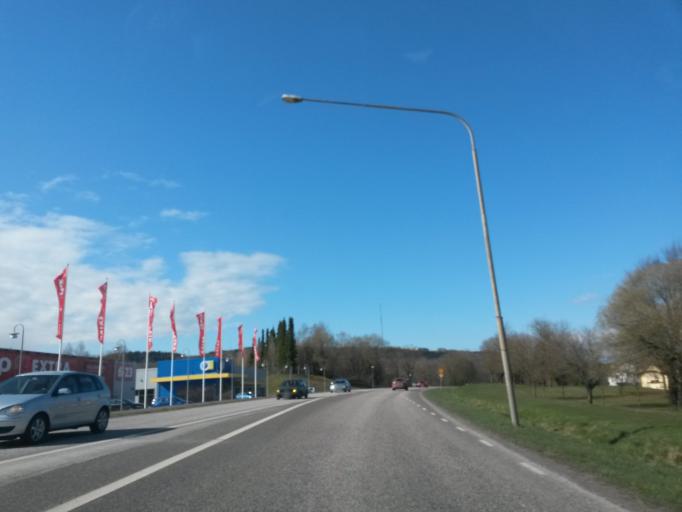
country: SE
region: Vaestra Goetaland
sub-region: Skovde Kommun
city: Skoevde
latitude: 58.3869
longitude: 13.8335
